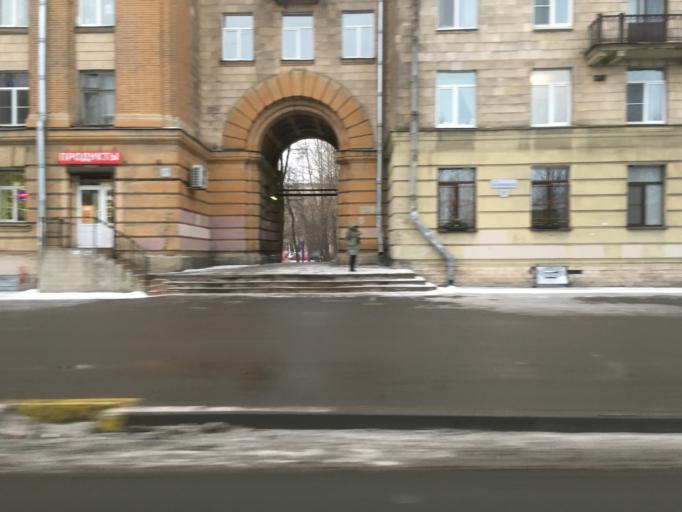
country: RU
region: St.-Petersburg
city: Obukhovo
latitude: 59.8770
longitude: 30.4374
